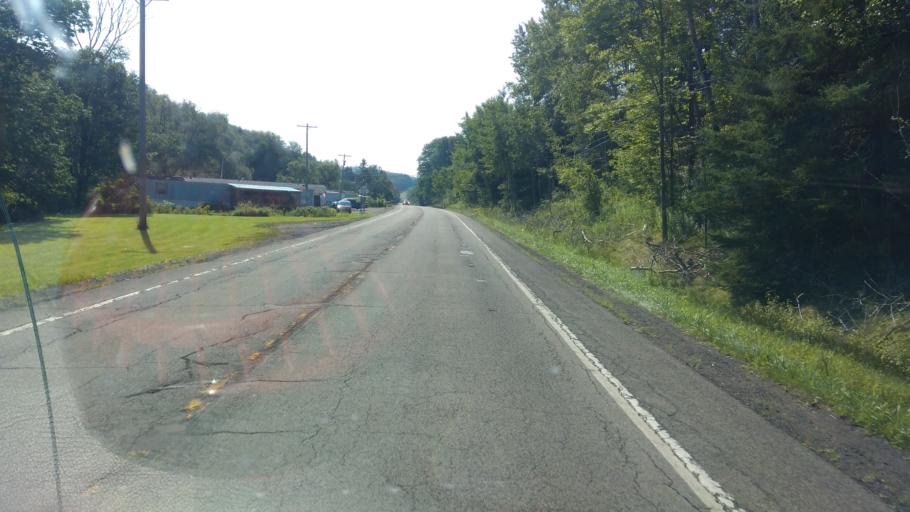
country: US
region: New York
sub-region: Allegany County
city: Cuba
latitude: 42.1907
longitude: -78.2659
